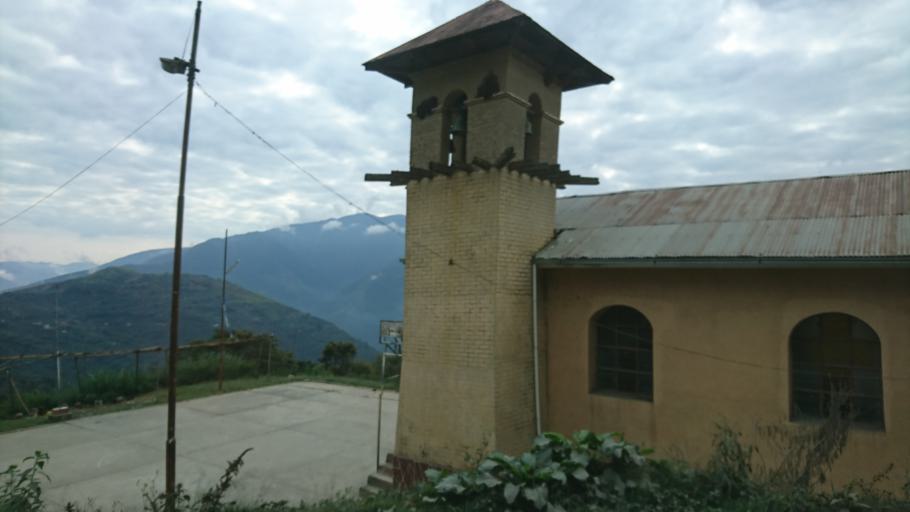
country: BO
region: La Paz
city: Coroico
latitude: -16.1968
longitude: -67.7080
